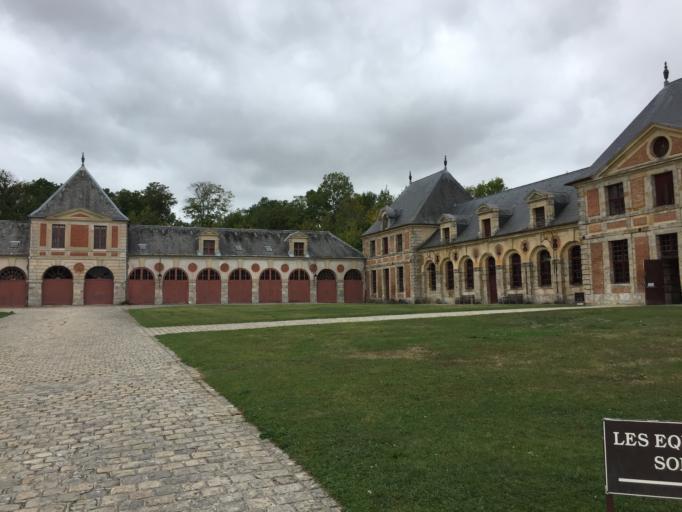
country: FR
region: Ile-de-France
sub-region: Departement de Seine-et-Marne
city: Maincy
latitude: 48.5672
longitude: 2.7129
